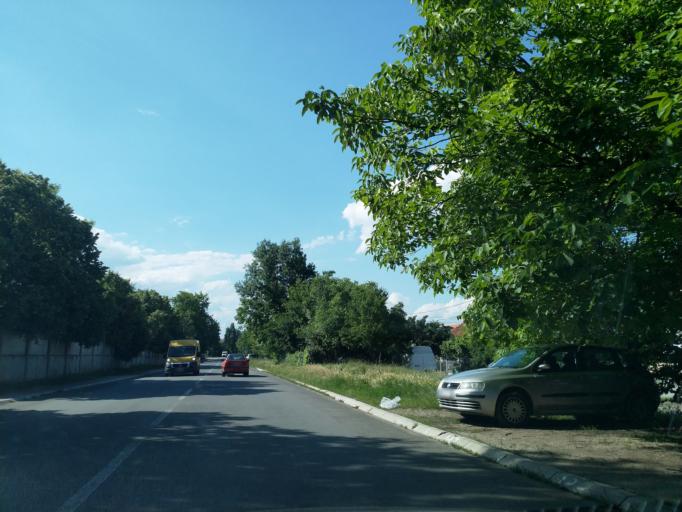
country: RS
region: Central Serbia
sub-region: Pomoravski Okrug
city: Paracin
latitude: 43.8542
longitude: 21.4083
